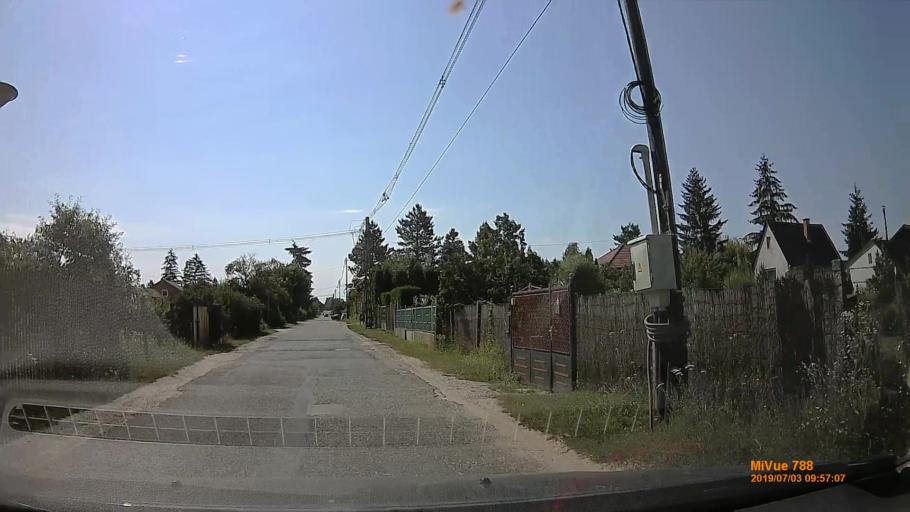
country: HU
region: Gyor-Moson-Sopron
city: Gyor
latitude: 47.7224
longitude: 17.7101
